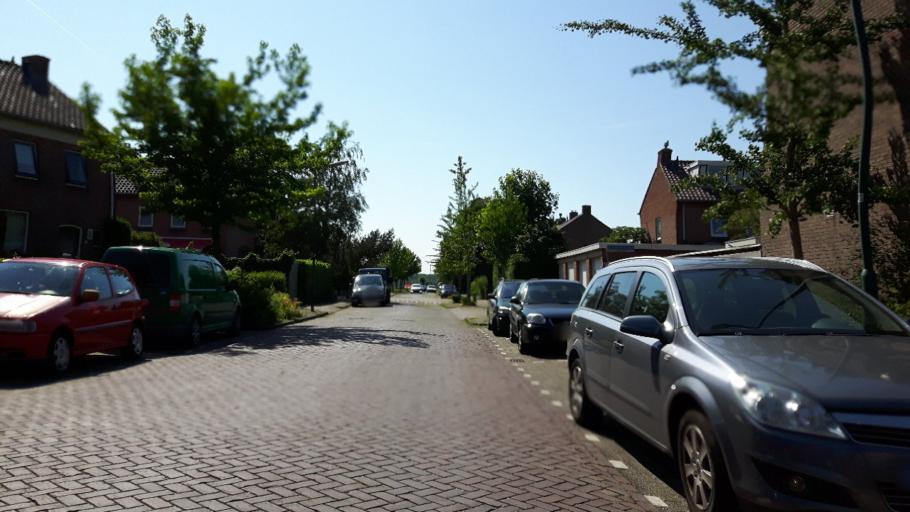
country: NL
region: Utrecht
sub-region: Stichtse Vecht
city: Vreeland
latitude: 52.2296
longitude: 5.0295
